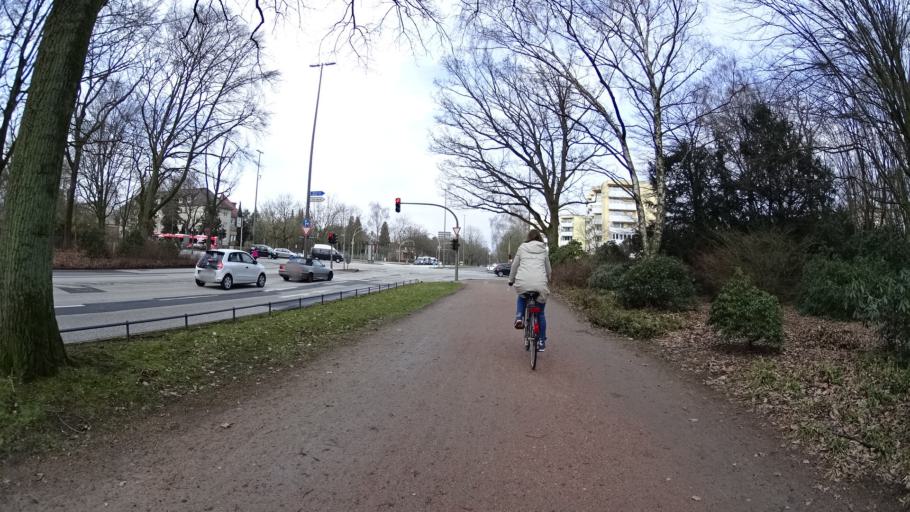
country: DE
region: Hamburg
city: Alsterdorf
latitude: 53.5994
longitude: 10.0140
